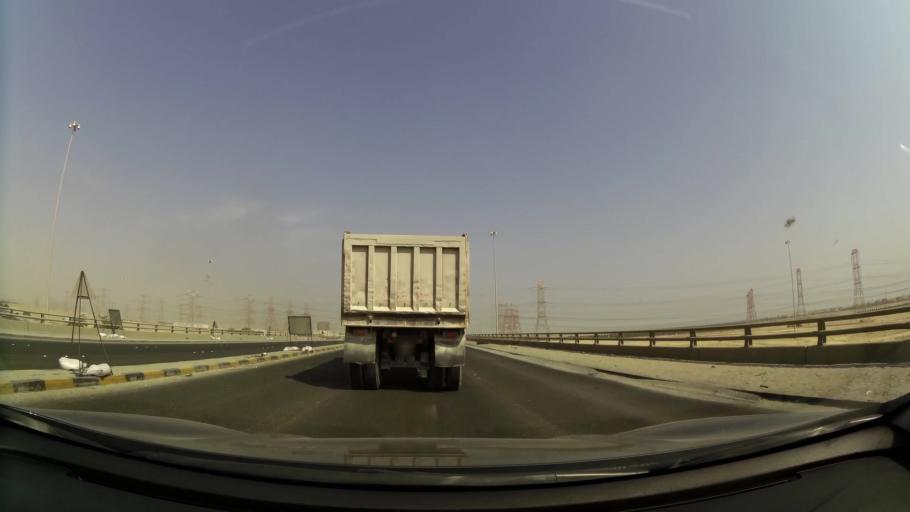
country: KW
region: Al Ahmadi
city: Al Fahahil
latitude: 28.9594
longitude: 48.1224
